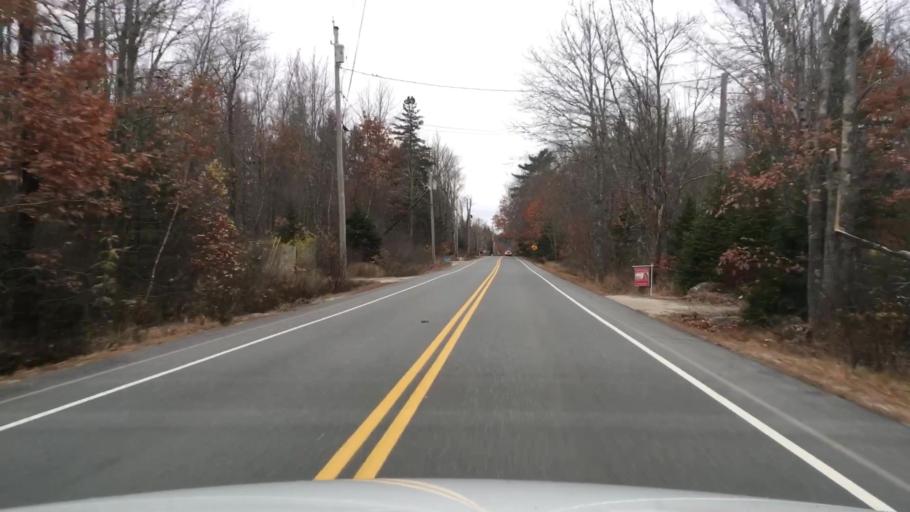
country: US
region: Maine
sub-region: Hancock County
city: Sedgwick
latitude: 44.4129
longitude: -68.6053
